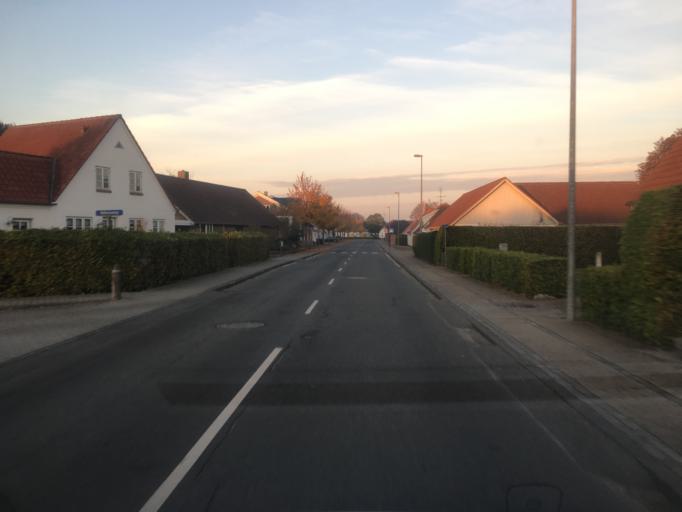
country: DK
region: South Denmark
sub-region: Tonder Kommune
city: Logumkloster
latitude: 55.0586
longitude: 8.9591
